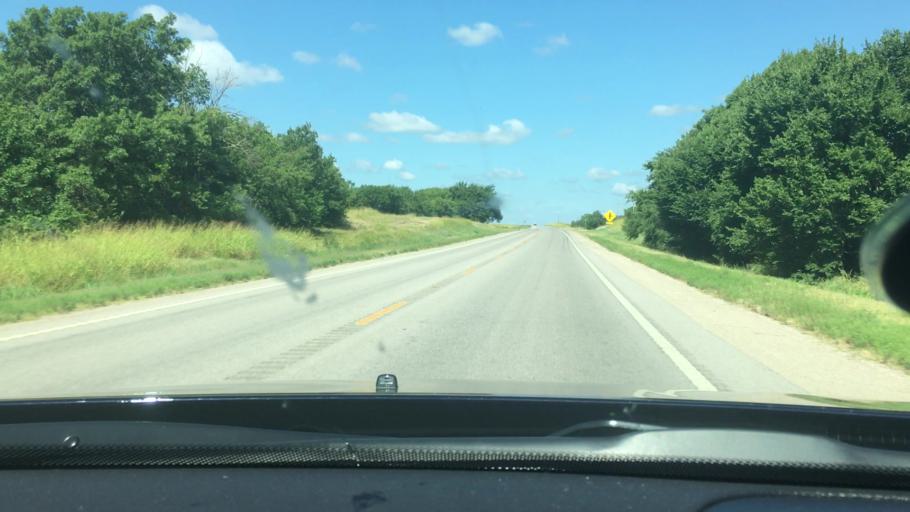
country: US
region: Oklahoma
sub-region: Marshall County
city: Oakland
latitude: 34.1001
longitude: -96.8255
